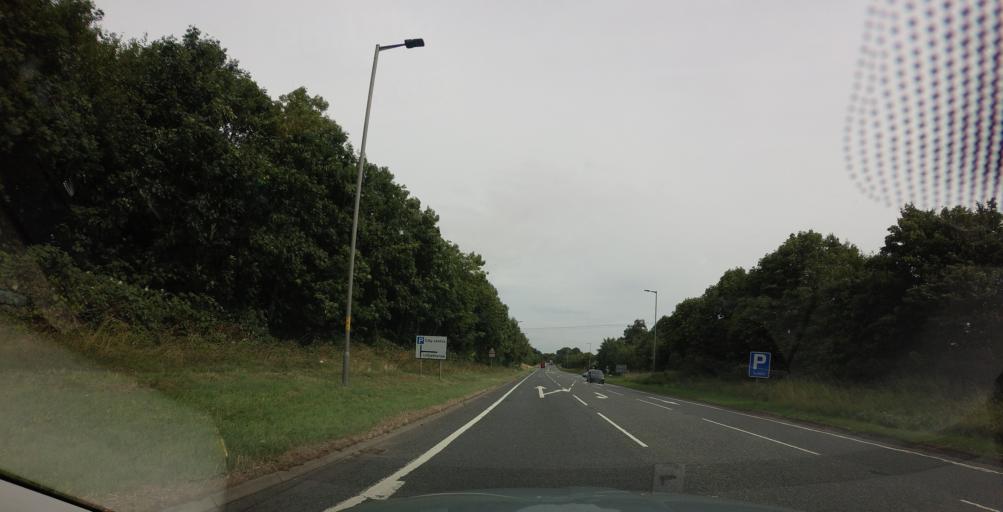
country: GB
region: England
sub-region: North Yorkshire
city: Ripon
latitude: 54.1243
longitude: -1.5180
